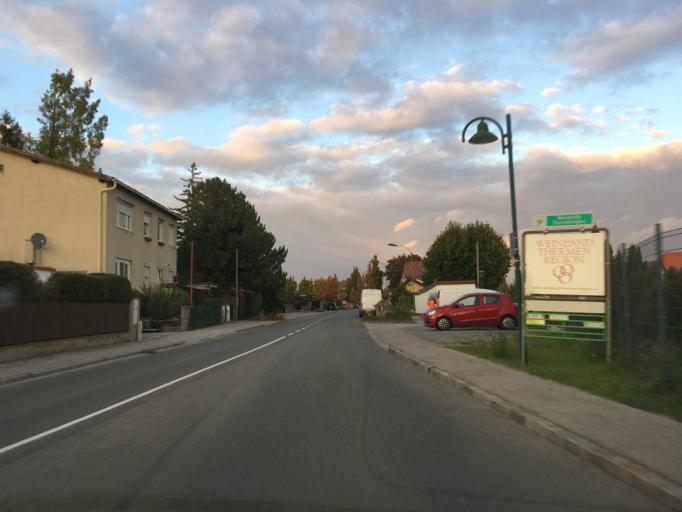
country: AT
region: Lower Austria
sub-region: Politischer Bezirk Baden
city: Pfaffstatten
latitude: 48.0163
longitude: 16.2545
